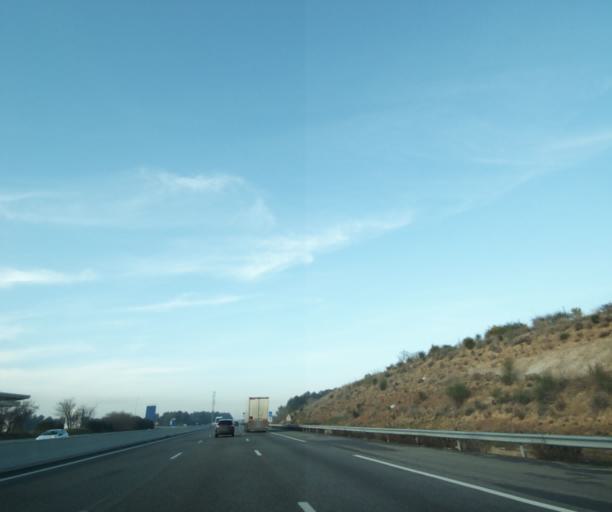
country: FR
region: Provence-Alpes-Cote d'Azur
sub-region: Departement des Bouches-du-Rhone
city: Peynier
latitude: 43.4704
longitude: 5.6546
